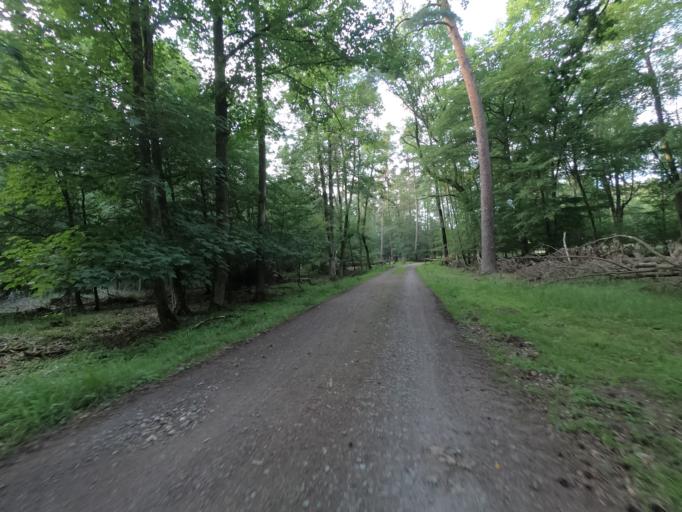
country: DE
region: Hesse
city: Raunheim
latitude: 49.9905
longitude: 8.4853
